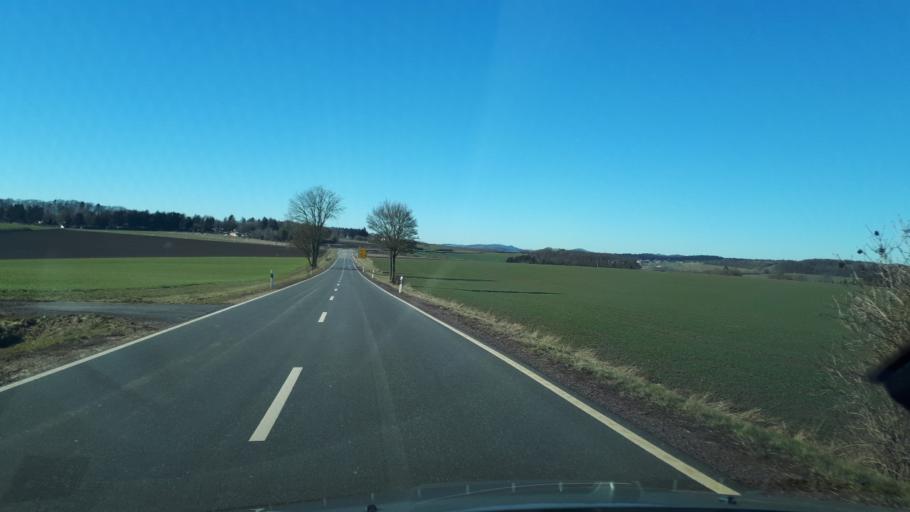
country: DE
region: Rheinland-Pfalz
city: Immerath
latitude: 50.1306
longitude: 6.9456
